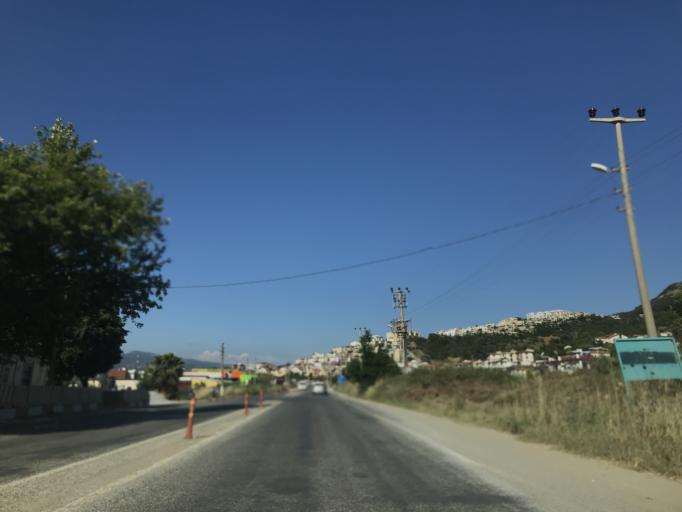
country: TR
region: Aydin
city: Davutlar
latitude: 37.7207
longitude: 27.2506
